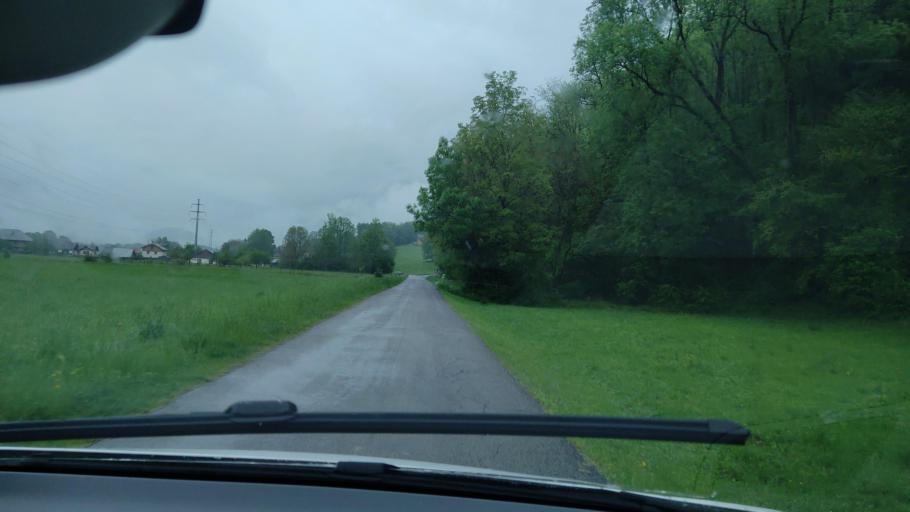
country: FR
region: Rhone-Alpes
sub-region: Departement de la Savoie
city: Saint-Remy-de-Maurienne
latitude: 45.4769
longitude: 6.2981
